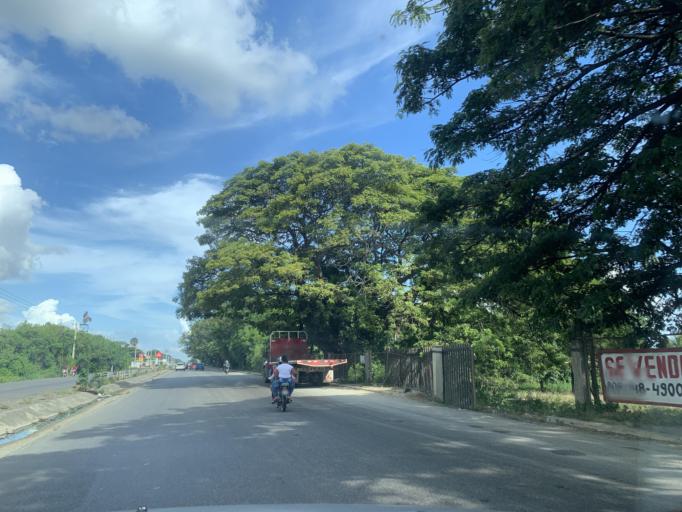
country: DO
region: Santiago
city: Villa Gonzalez
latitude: 19.5461
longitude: -70.8062
